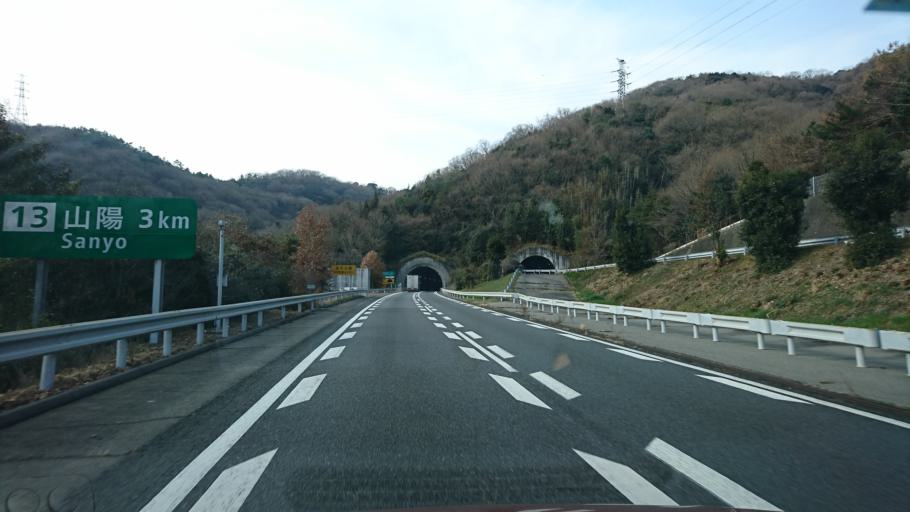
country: JP
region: Okayama
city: Okayama-shi
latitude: 34.7588
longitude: 134.0547
